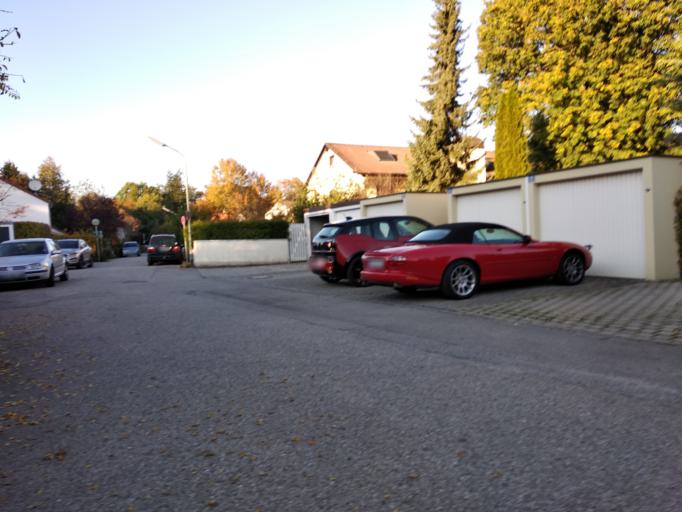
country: DE
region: Bavaria
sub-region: Upper Bavaria
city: Vaterstetten
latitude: 48.1084
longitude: 11.7604
